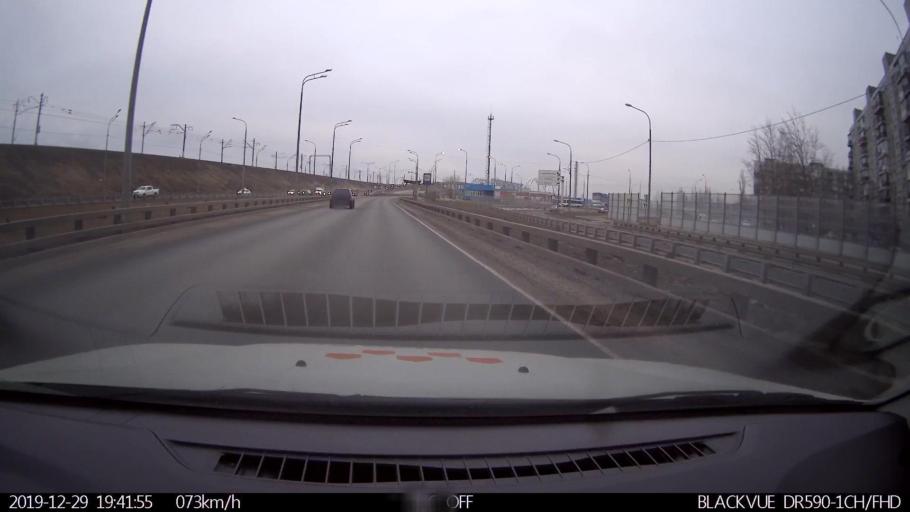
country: RU
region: Nizjnij Novgorod
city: Nizhniy Novgorod
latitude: 56.3443
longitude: 43.9223
